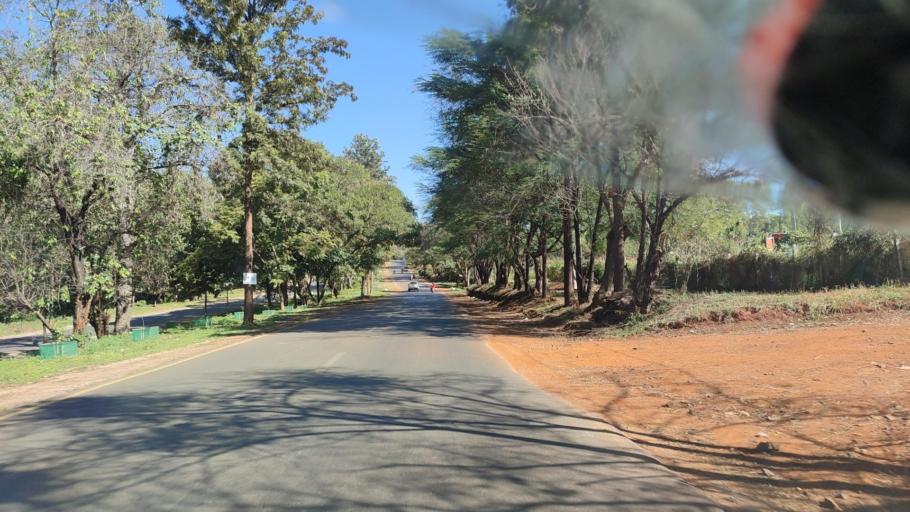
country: MM
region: Mandalay
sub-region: Pyin Oo Lwin District
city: Pyin Oo Lwin
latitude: 21.9861
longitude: 96.4171
